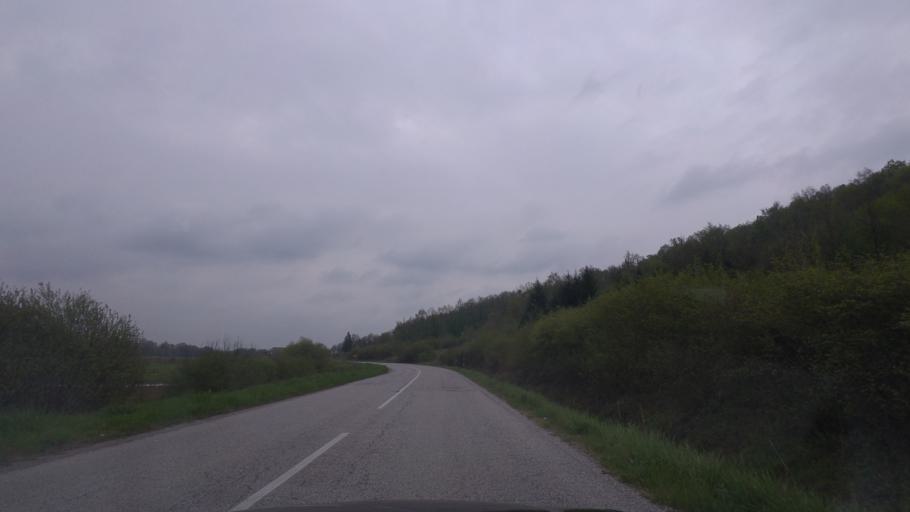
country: HR
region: Karlovacka
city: Ozalj
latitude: 45.6399
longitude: 15.5325
